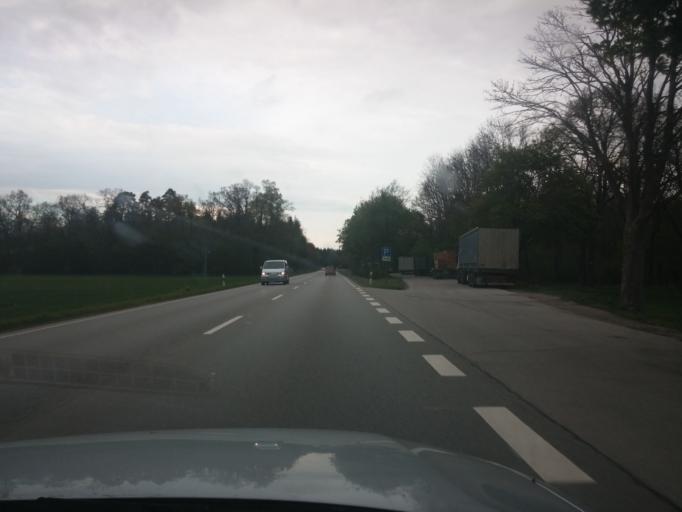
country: DE
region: Bavaria
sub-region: Upper Bavaria
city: Putzbrunn
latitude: 48.0878
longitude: 11.7206
